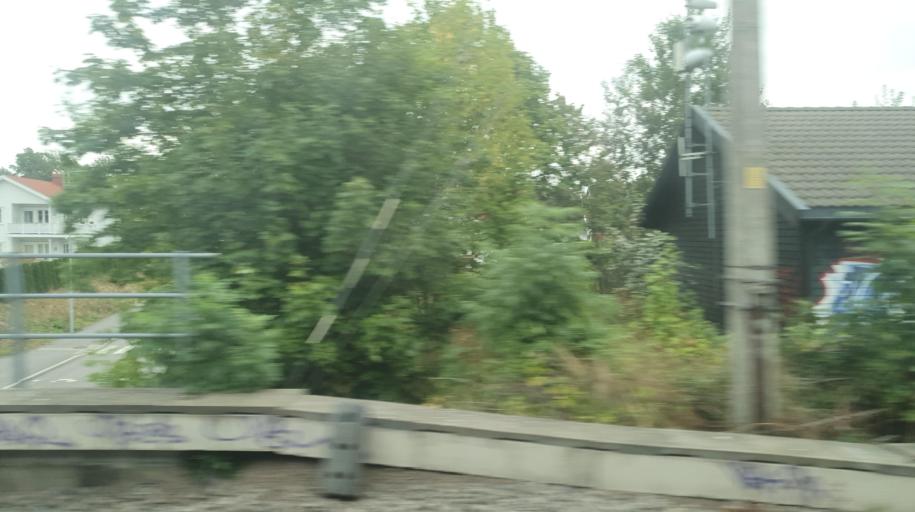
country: NO
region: Vestfold
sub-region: Tonsberg
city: Tonsberg
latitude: 59.2763
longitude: 10.4076
